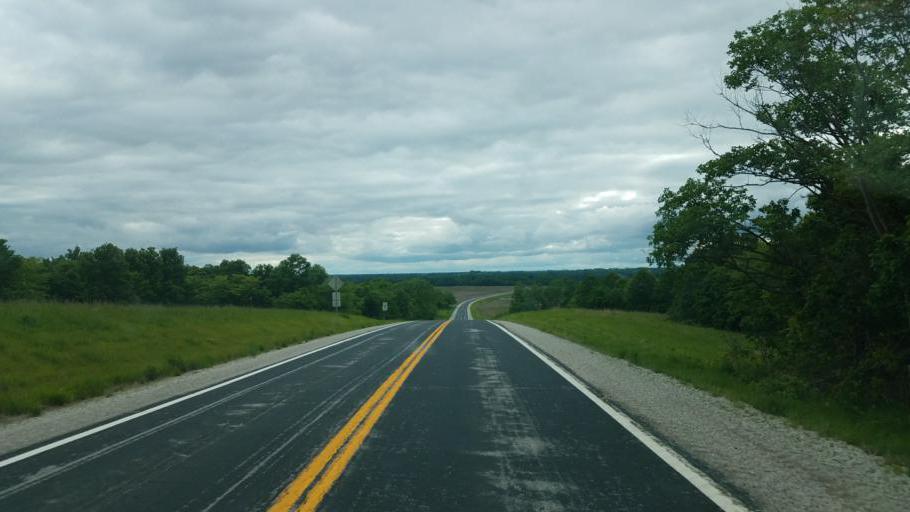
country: US
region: Missouri
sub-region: Mercer County
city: Princeton
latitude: 40.3395
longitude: -93.7492
